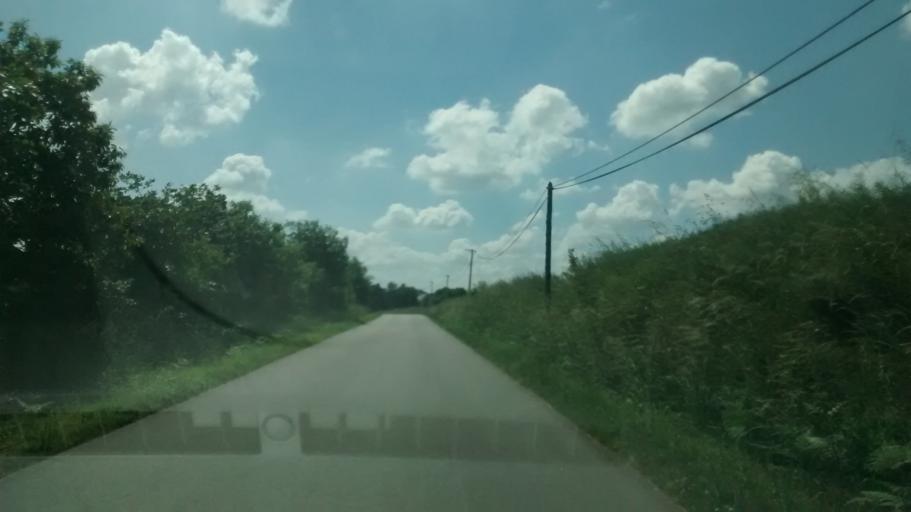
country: FR
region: Brittany
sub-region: Departement du Morbihan
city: Caro
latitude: 47.8755
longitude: -2.2959
